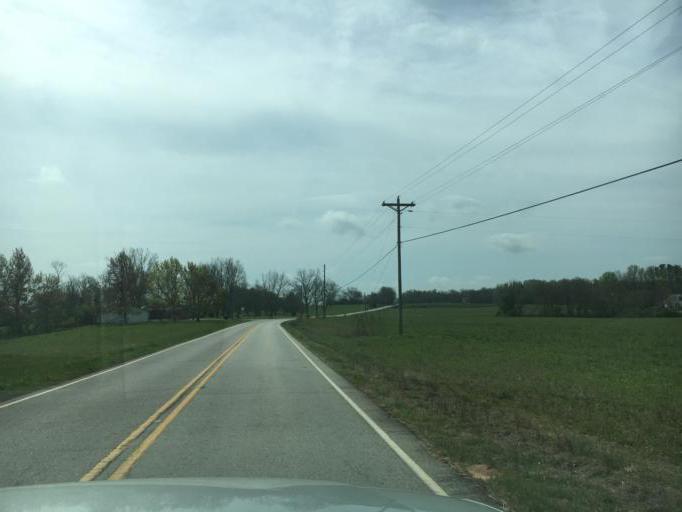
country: US
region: Georgia
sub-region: Hart County
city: Royston
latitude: 34.3380
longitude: -83.0389
